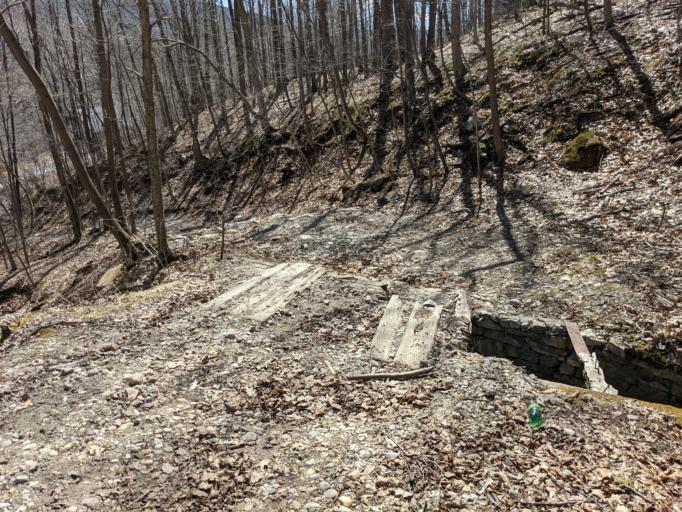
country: US
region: Vermont
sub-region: Bennington County
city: Manchester Center
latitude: 43.2413
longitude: -73.0136
